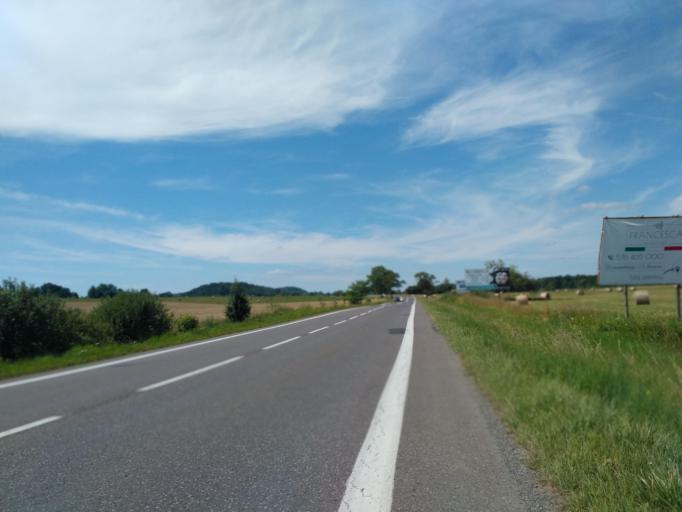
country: PL
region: Subcarpathian Voivodeship
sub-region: Powiat sanocki
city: Strachocina
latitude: 49.6054
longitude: 22.1296
